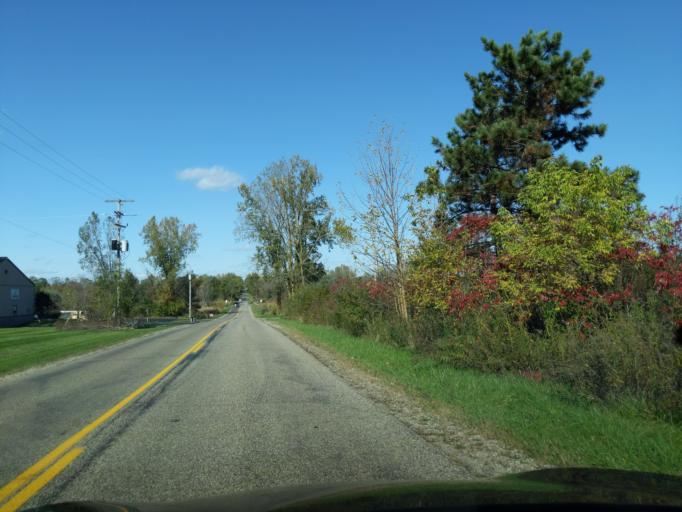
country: US
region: Michigan
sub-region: Eaton County
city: Charlotte
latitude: 42.5999
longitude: -84.7979
